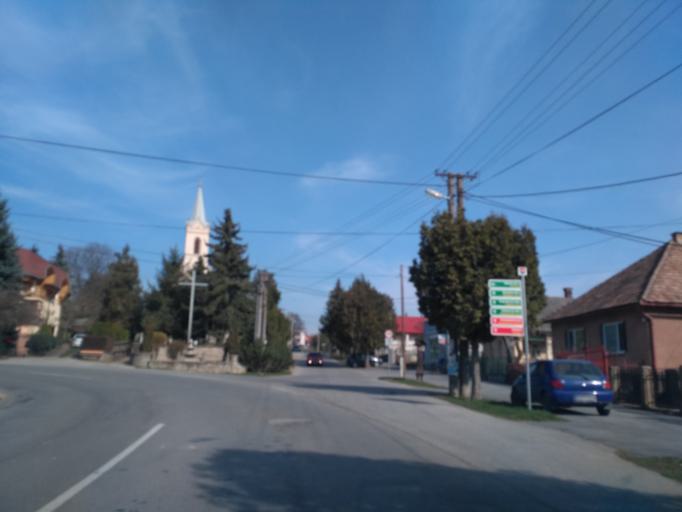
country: SK
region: Kosicky
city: Moldava nad Bodvou
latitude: 48.5973
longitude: 21.0209
